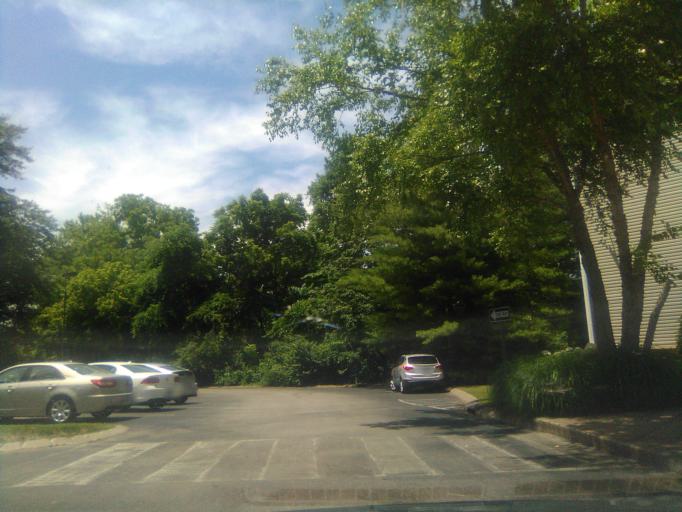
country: US
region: Tennessee
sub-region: Davidson County
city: Belle Meade
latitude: 36.1288
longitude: -86.8497
